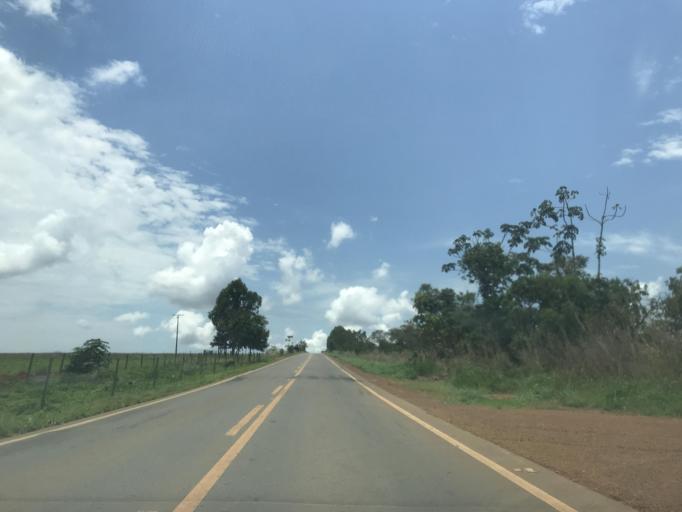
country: BR
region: Goias
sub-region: Luziania
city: Luziania
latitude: -16.4846
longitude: -48.2030
